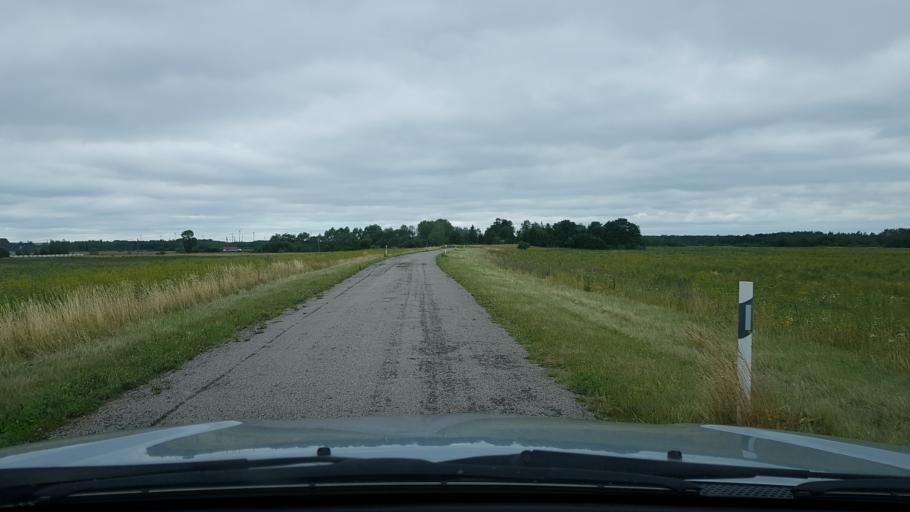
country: EE
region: Ida-Virumaa
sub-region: Narva linn
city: Narva
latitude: 59.3855
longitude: 28.1426
